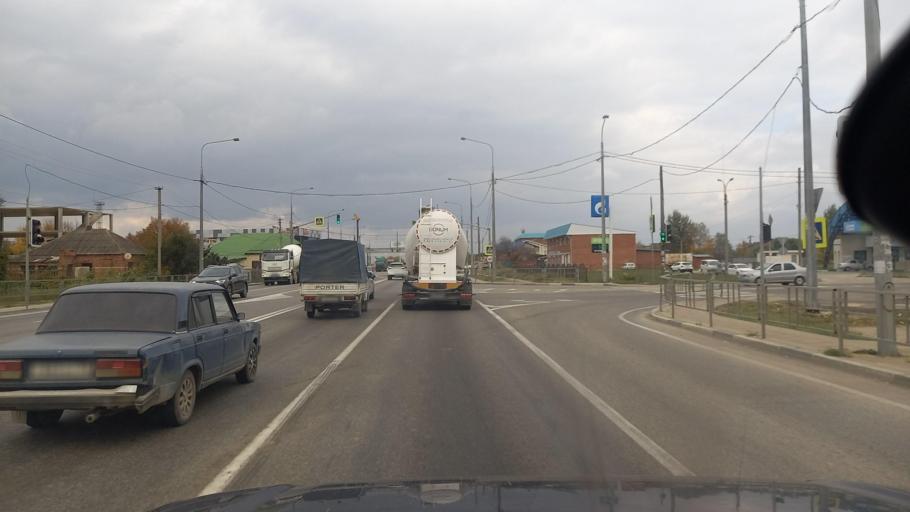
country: RU
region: Adygeya
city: Enem
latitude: 44.9302
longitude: 38.9104
